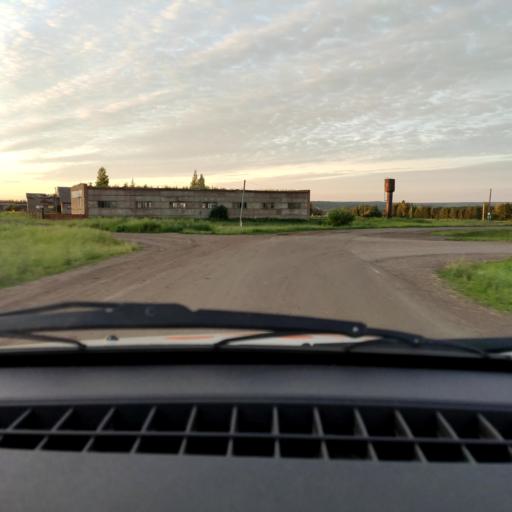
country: RU
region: Bashkortostan
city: Avdon
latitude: 54.5121
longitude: 55.7745
